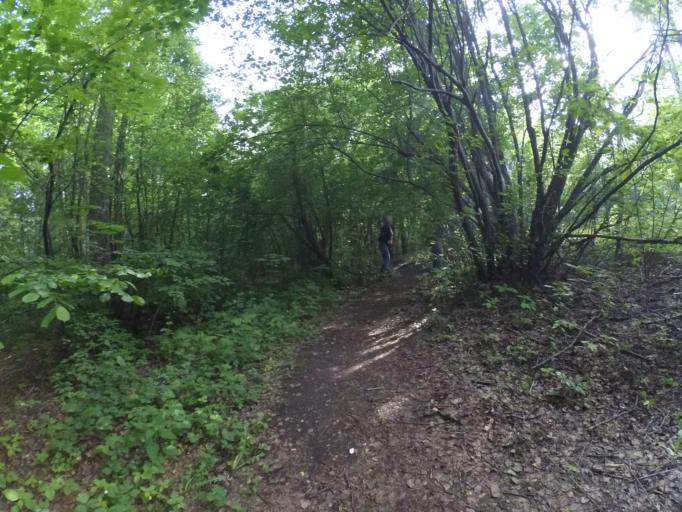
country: RU
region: Moscow
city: Pokrovskoye-Streshnevo
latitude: 55.8233
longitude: 37.4625
